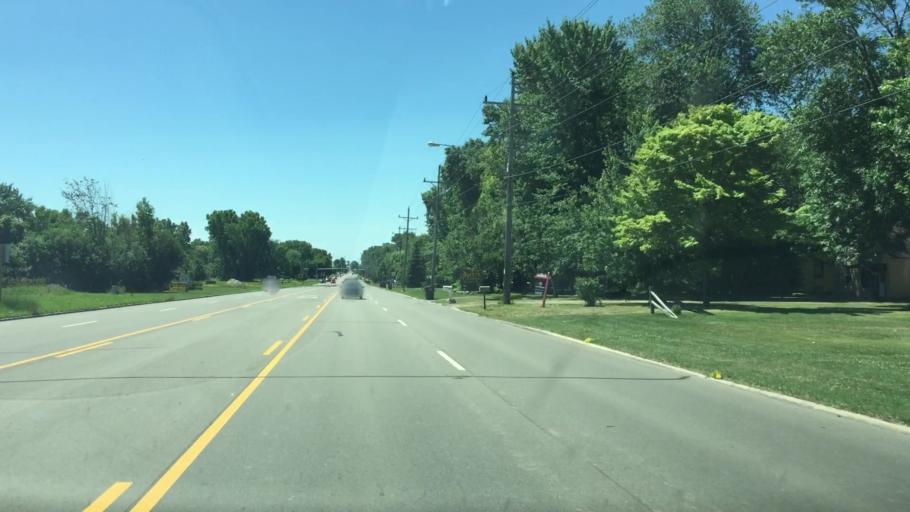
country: US
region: Wisconsin
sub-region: Outagamie County
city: Appleton
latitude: 44.2231
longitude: -88.4042
